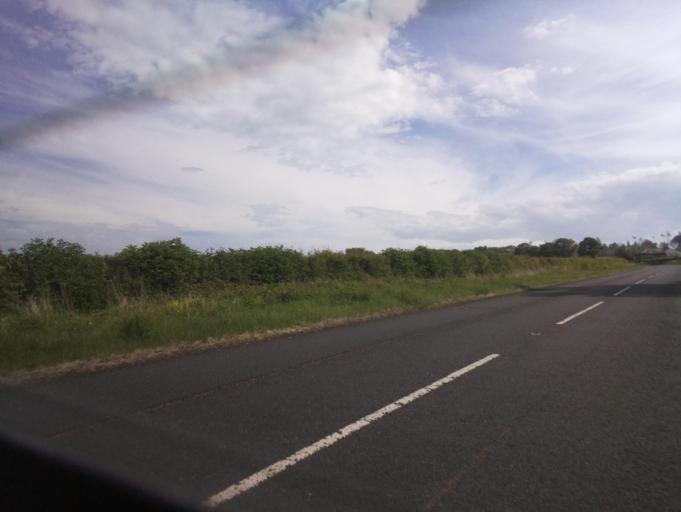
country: GB
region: England
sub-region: Northumberland
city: Alnwick
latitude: 55.4600
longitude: -1.7152
